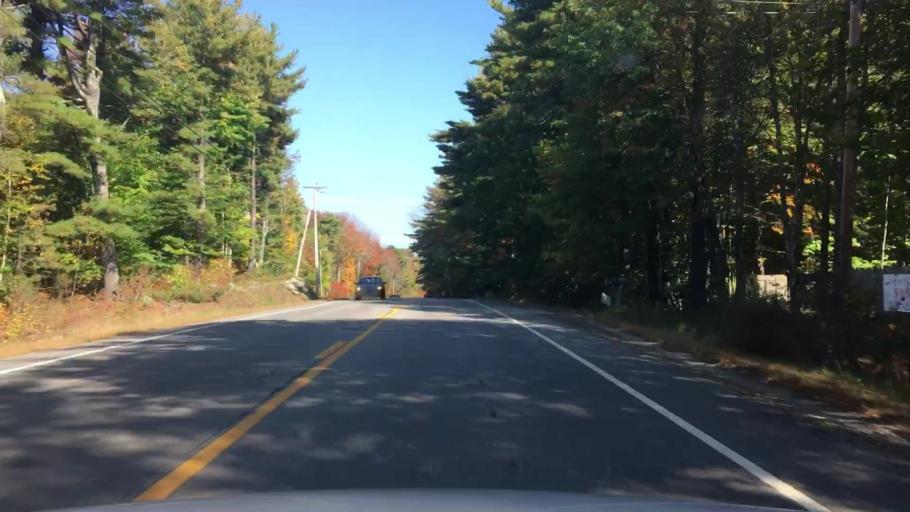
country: US
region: Maine
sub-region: Sagadahoc County
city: Topsham
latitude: 44.0040
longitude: -69.9492
